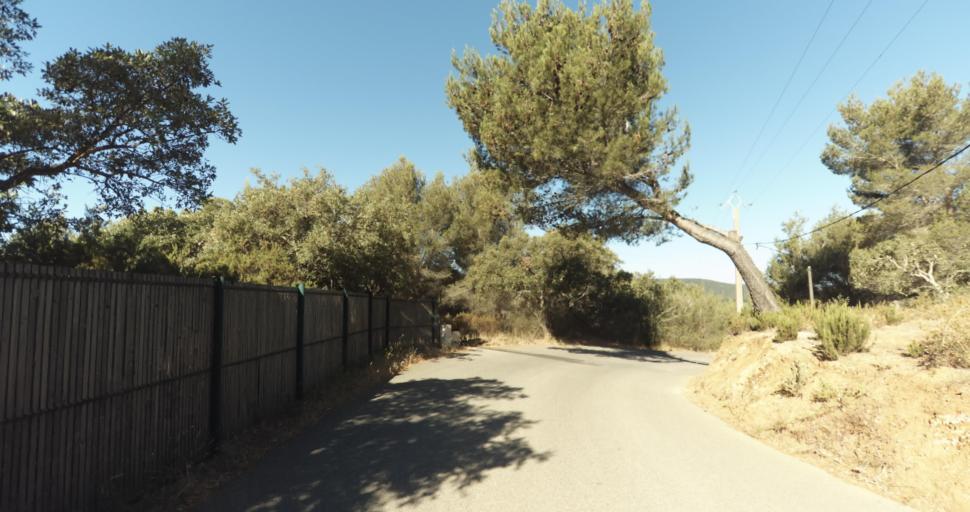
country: FR
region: Provence-Alpes-Cote d'Azur
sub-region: Departement du Var
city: Gassin
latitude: 43.2156
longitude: 6.5870
